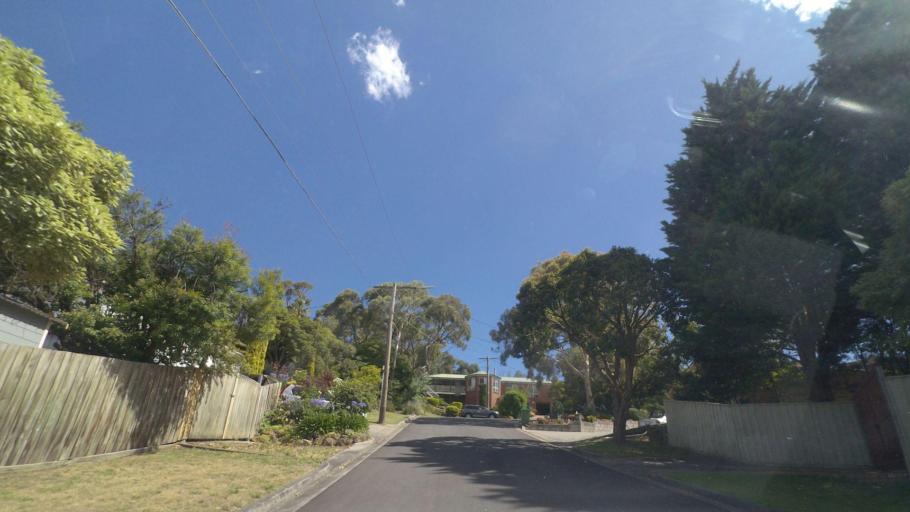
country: AU
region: Victoria
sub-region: Yarra Ranges
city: Kilsyth
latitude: -37.8056
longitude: 145.3343
